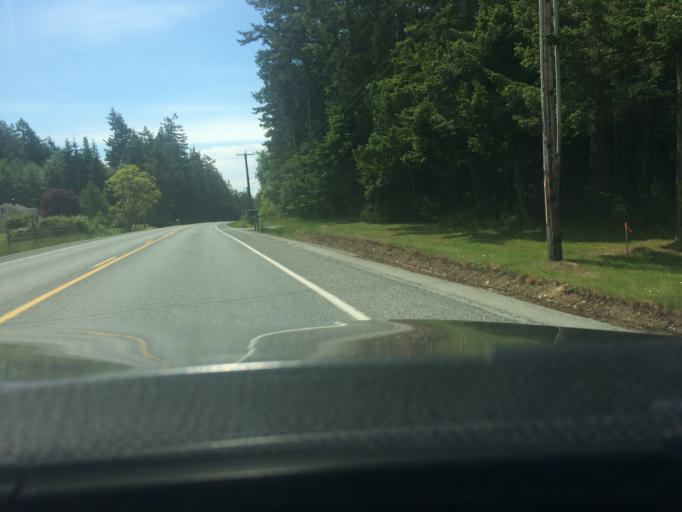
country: US
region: Washington
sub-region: Island County
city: Ault Field
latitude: 48.4305
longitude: -122.6641
